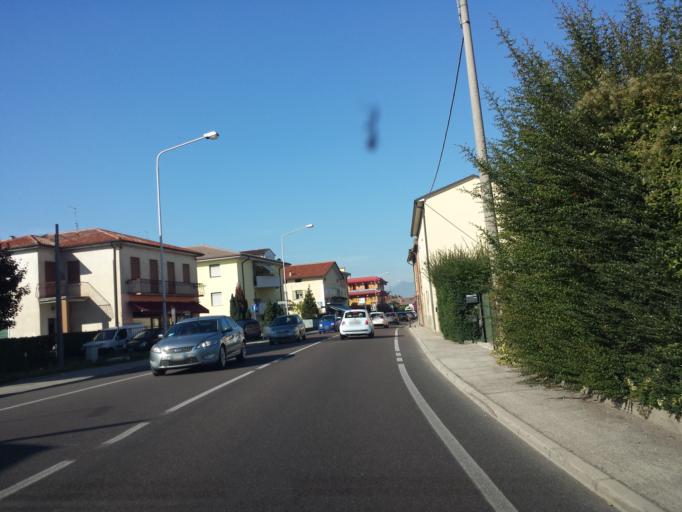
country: IT
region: Veneto
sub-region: Provincia di Vicenza
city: Crispi Cavour
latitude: 45.5743
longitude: 11.5110
